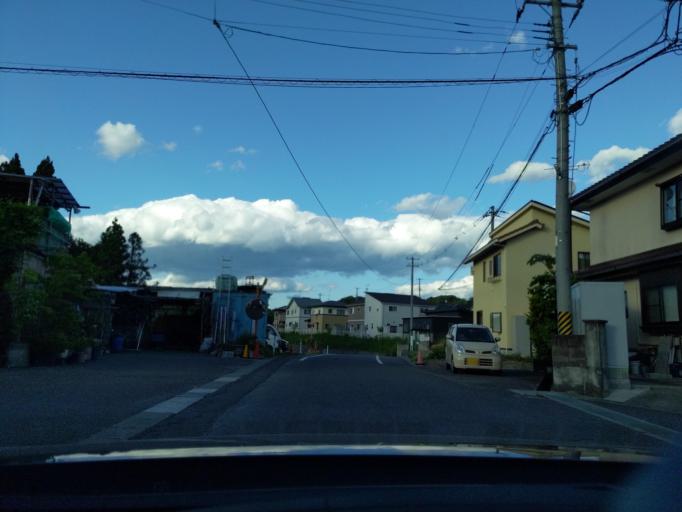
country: JP
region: Fukushima
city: Miharu
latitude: 37.4278
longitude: 140.4338
